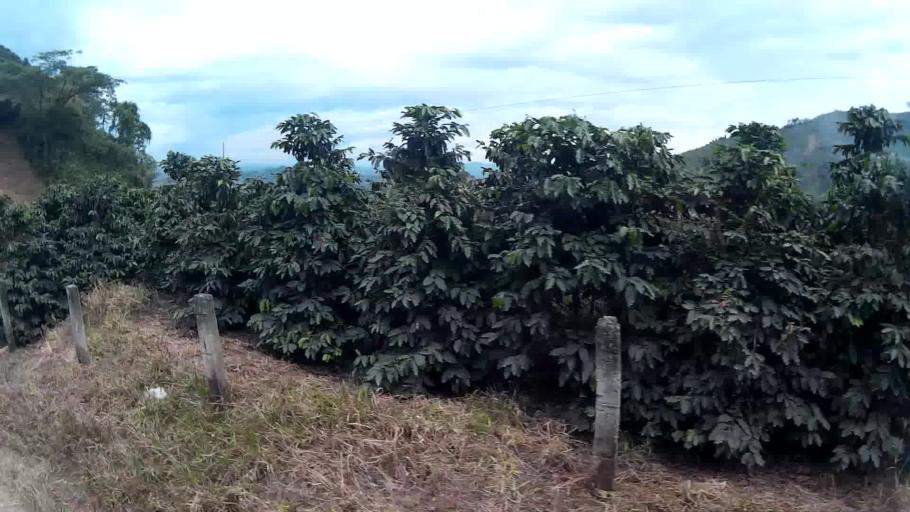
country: CO
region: Risaralda
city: Marsella
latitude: 4.8694
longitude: -75.7610
